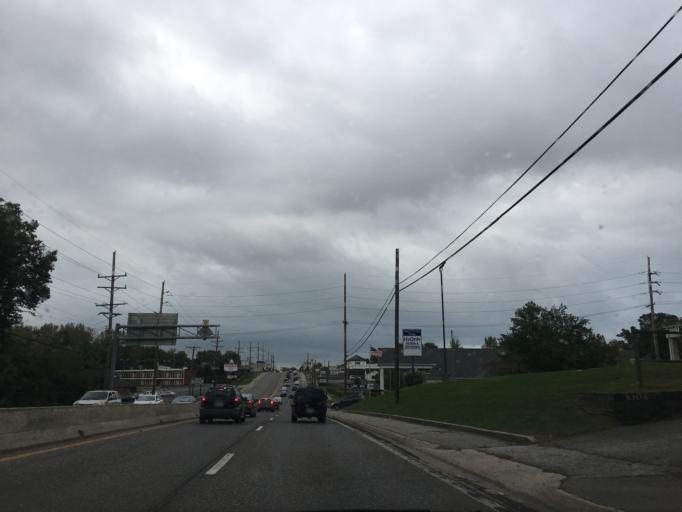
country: US
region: Missouri
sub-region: Saint Louis County
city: Saint Ann
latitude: 38.7251
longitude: -90.4064
